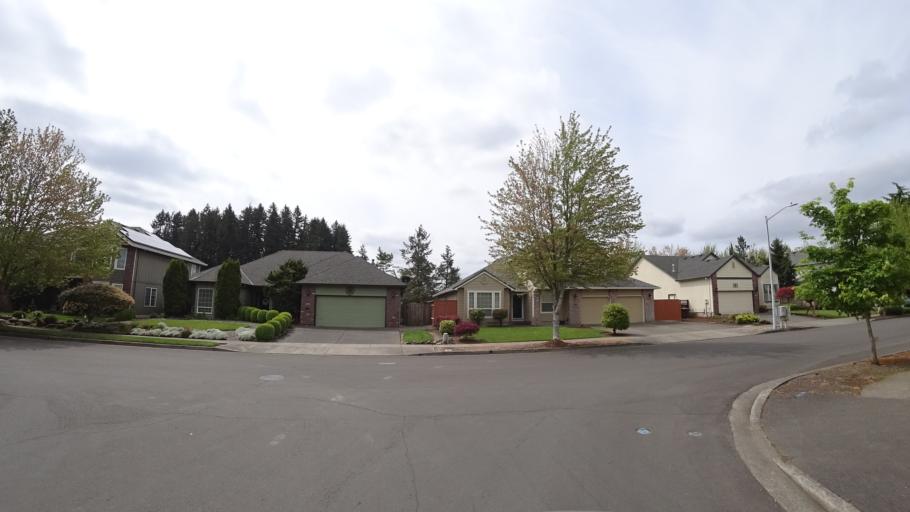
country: US
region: Oregon
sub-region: Washington County
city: Hillsboro
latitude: 45.5439
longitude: -122.9921
